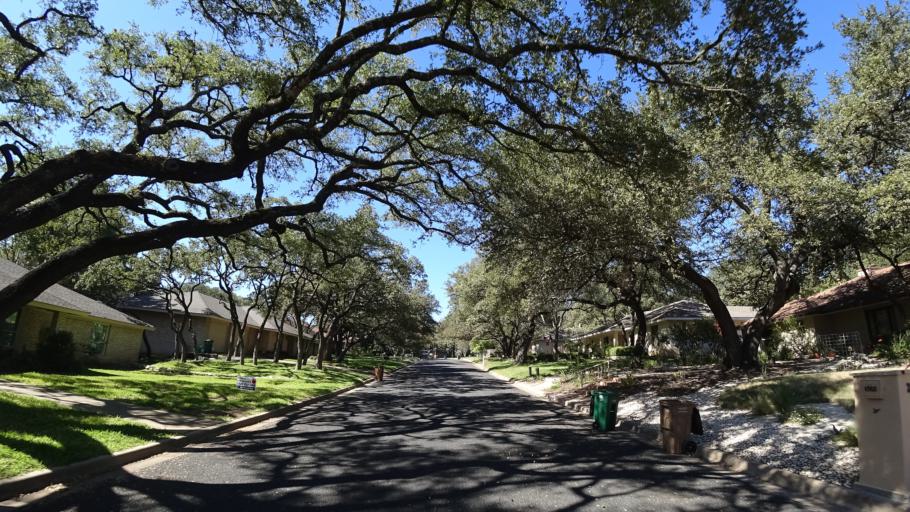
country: US
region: Texas
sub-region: Travis County
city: West Lake Hills
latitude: 30.3645
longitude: -97.7585
